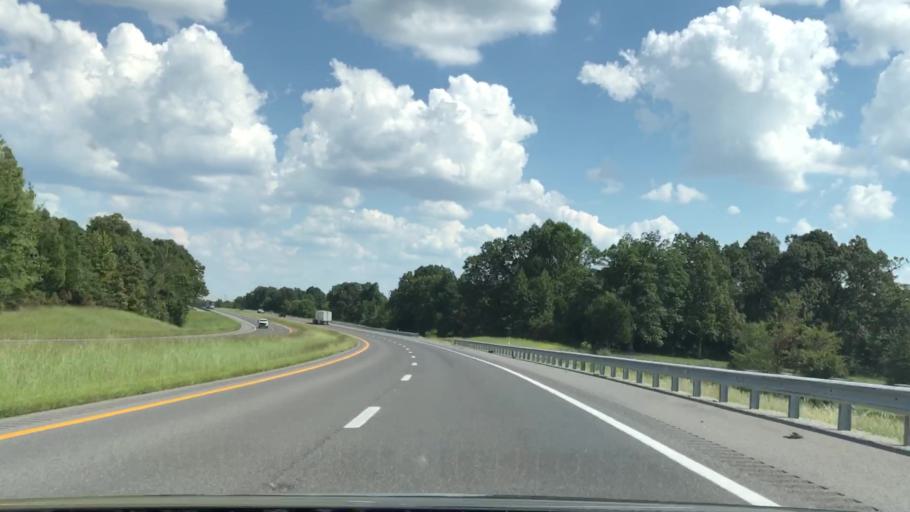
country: US
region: Kentucky
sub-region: Lyon County
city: Eddyville
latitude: 37.1066
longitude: -87.9876
